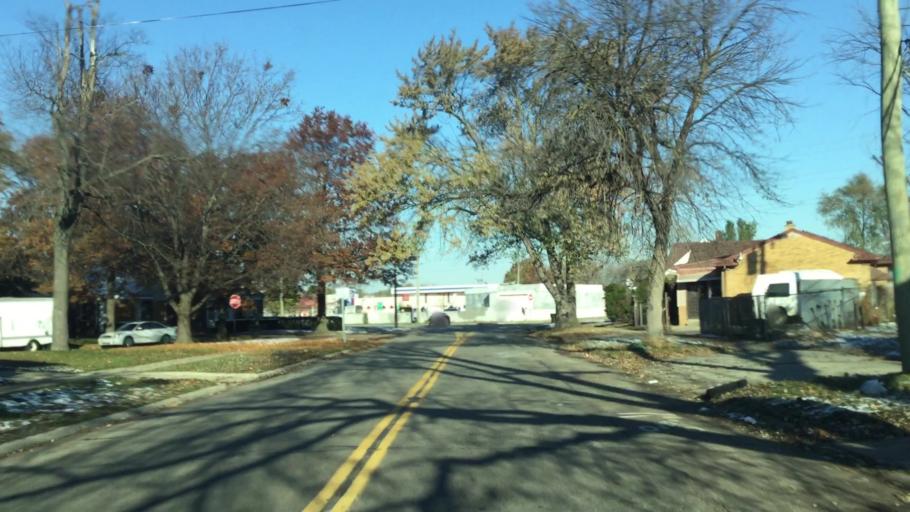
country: US
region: Michigan
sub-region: Macomb County
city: Warren
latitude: 42.4468
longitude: -83.0220
